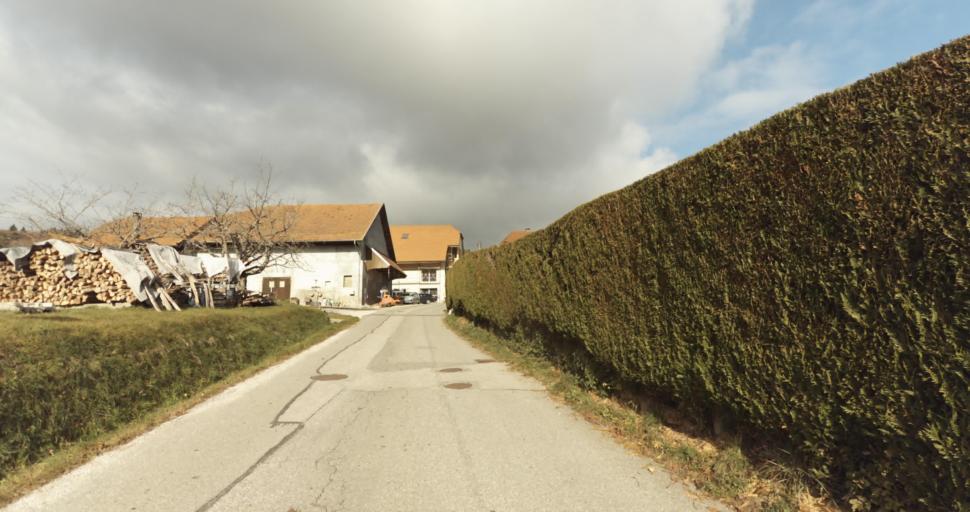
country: FR
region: Rhone-Alpes
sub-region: Departement de la Haute-Savoie
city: Epagny
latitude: 45.9686
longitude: 6.0874
